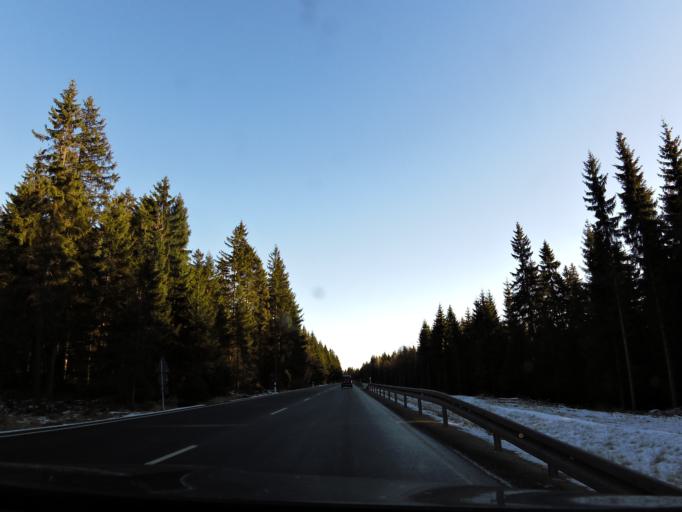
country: DE
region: Bavaria
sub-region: Upper Franconia
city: Fichtelberg
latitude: 50.0247
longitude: 11.8620
